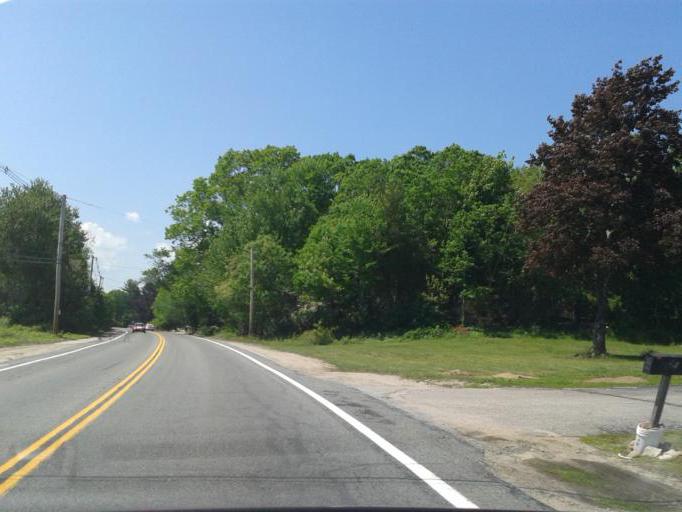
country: US
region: Rhode Island
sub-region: Washington County
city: Hope Valley
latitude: 41.5086
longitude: -71.6820
